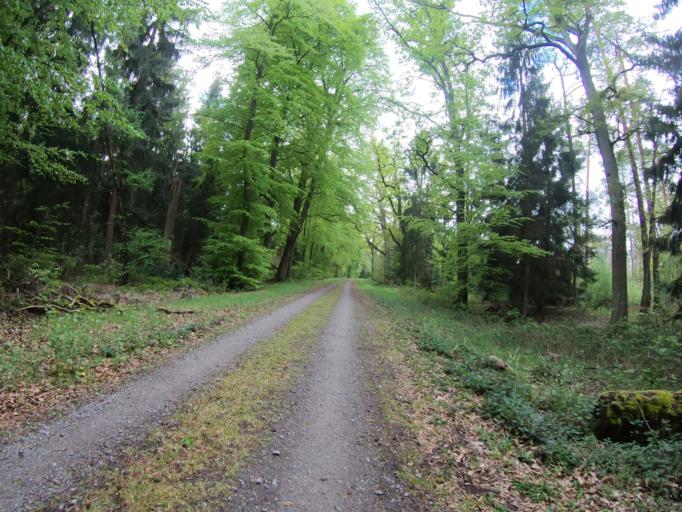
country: DE
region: Lower Saxony
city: Gifhorn
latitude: 52.5015
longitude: 10.5667
